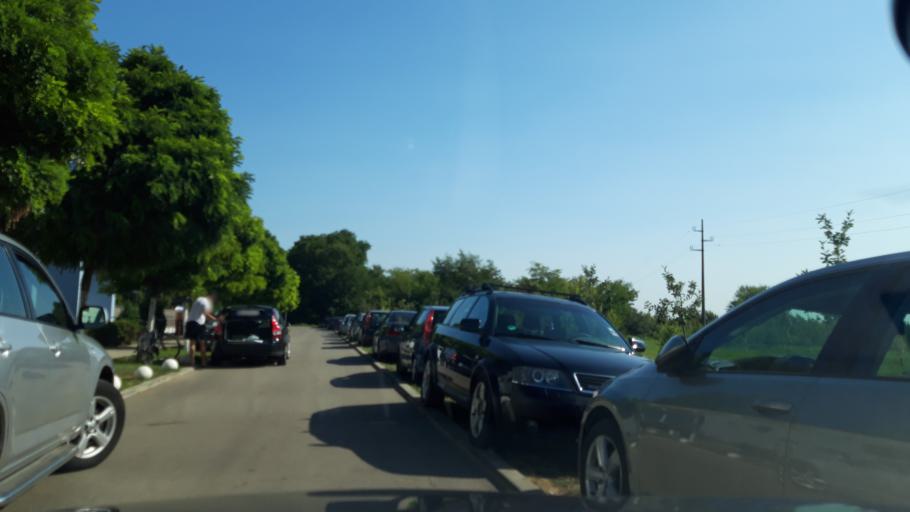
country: RS
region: Autonomna Pokrajina Vojvodina
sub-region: Sremski Okrug
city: Ruma
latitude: 45.0345
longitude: 19.8178
